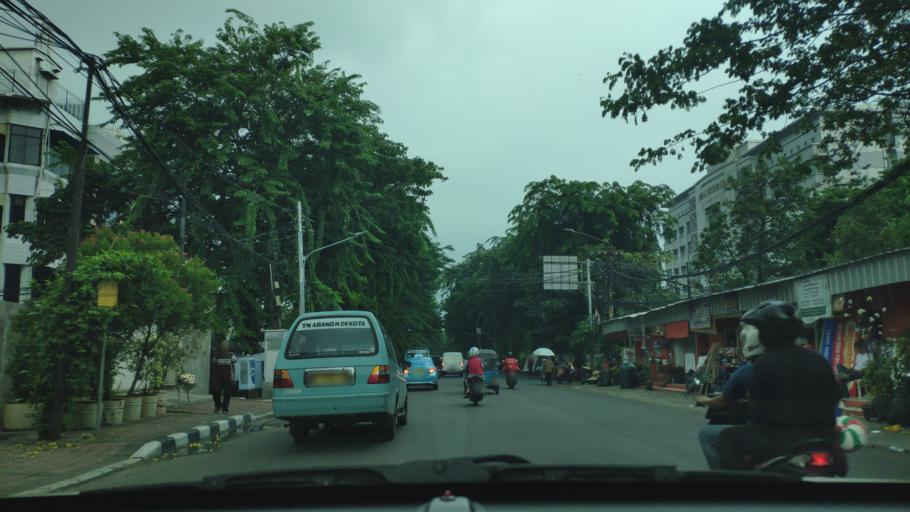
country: ID
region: Jakarta Raya
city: Jakarta
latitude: -6.1708
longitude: 106.8149
